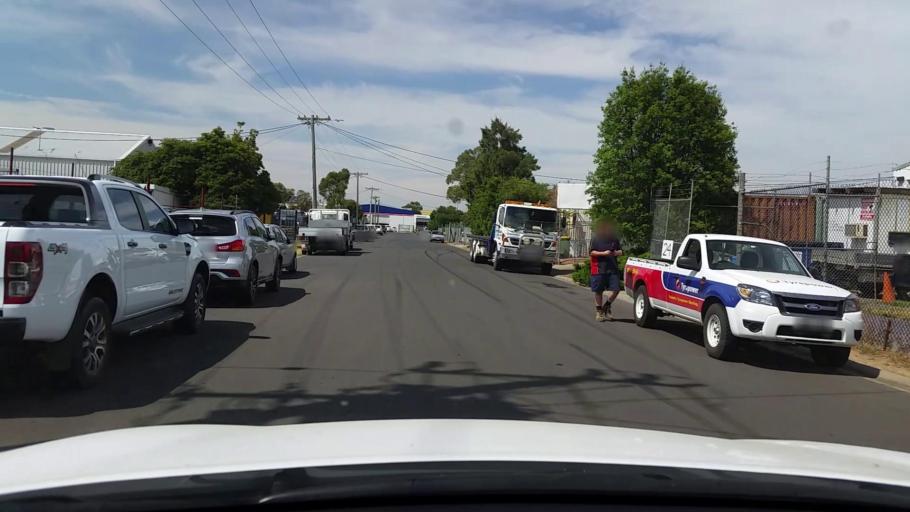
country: AU
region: Victoria
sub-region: Mornington Peninsula
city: Hastings
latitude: -38.3053
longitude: 145.1847
